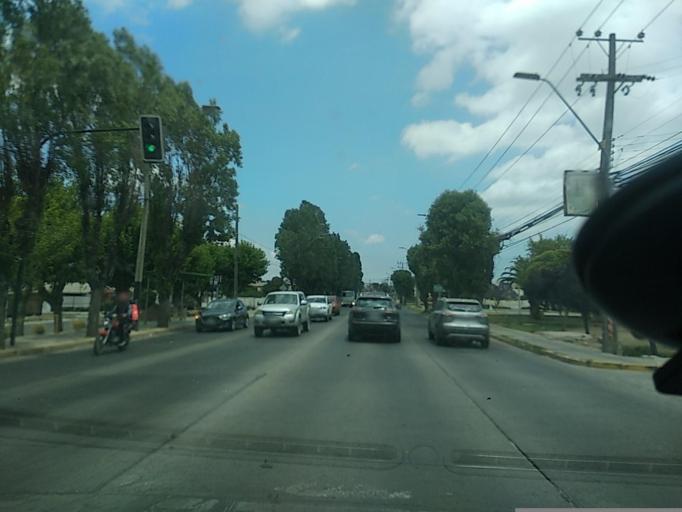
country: CL
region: Valparaiso
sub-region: Provincia de Marga Marga
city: Villa Alemana
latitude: -33.0461
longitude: -71.3939
